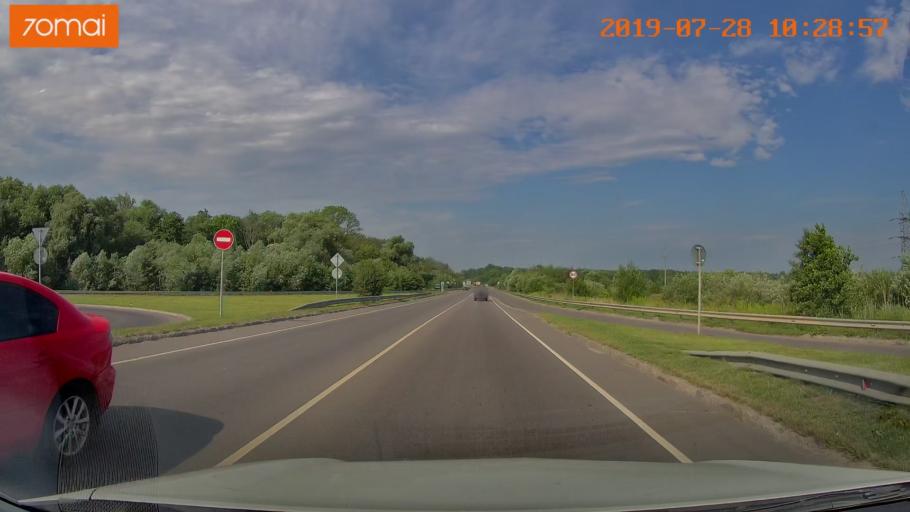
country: RU
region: Kaliningrad
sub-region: Gorod Kaliningrad
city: Kaliningrad
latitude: 54.7667
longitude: 20.4907
